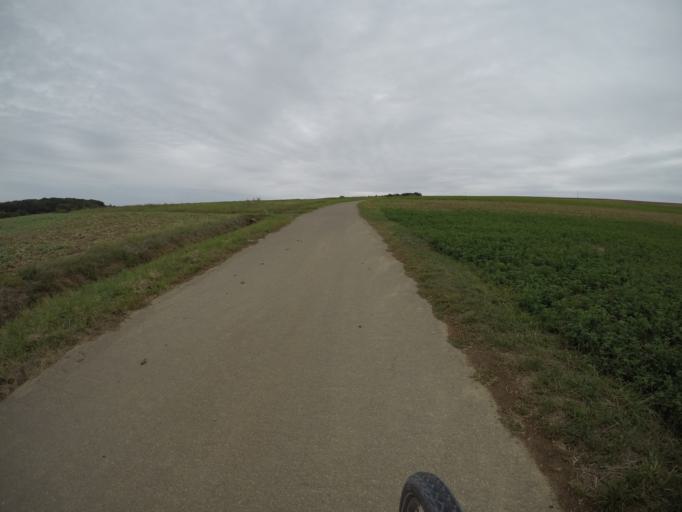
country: DE
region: Baden-Wuerttemberg
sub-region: Regierungsbezirk Stuttgart
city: Eberdingen
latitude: 48.8915
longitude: 8.9747
